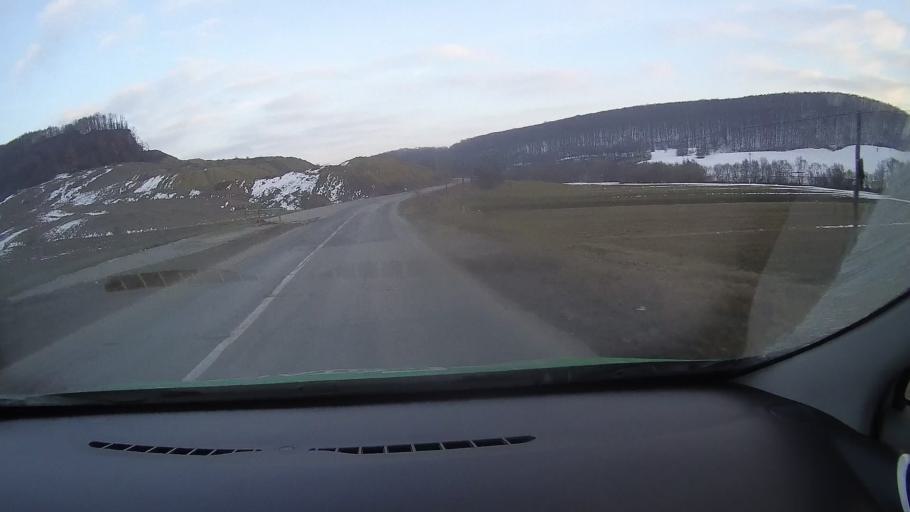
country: RO
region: Harghita
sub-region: Comuna Lupeni
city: Lupeni
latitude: 46.3601
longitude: 25.1883
